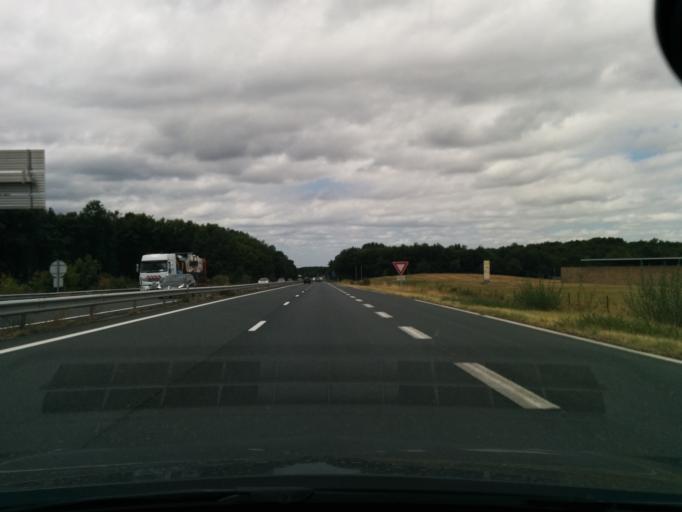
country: FR
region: Centre
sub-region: Departement de l'Indre
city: Argenton-sur-Creuse
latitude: 46.5733
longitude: 1.4993
